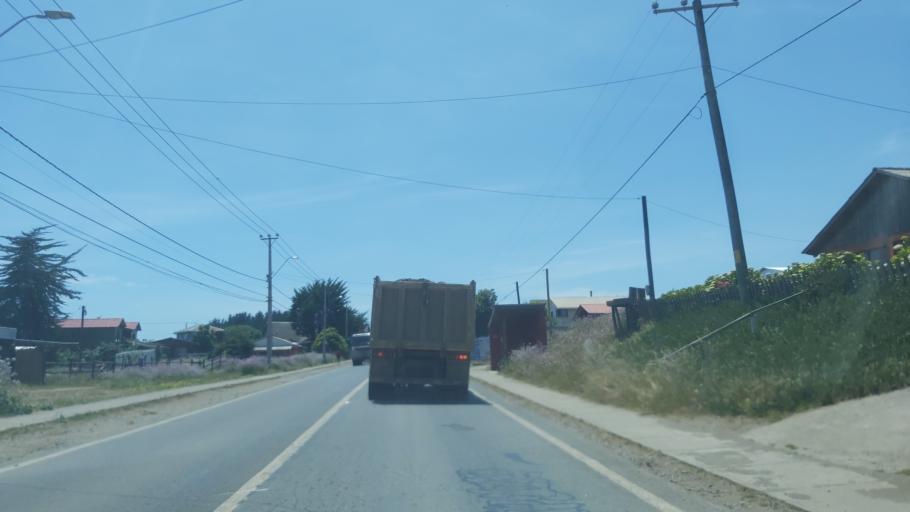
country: CL
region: Maule
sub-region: Provincia de Cauquenes
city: Cauquenes
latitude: -35.8028
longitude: -72.5660
